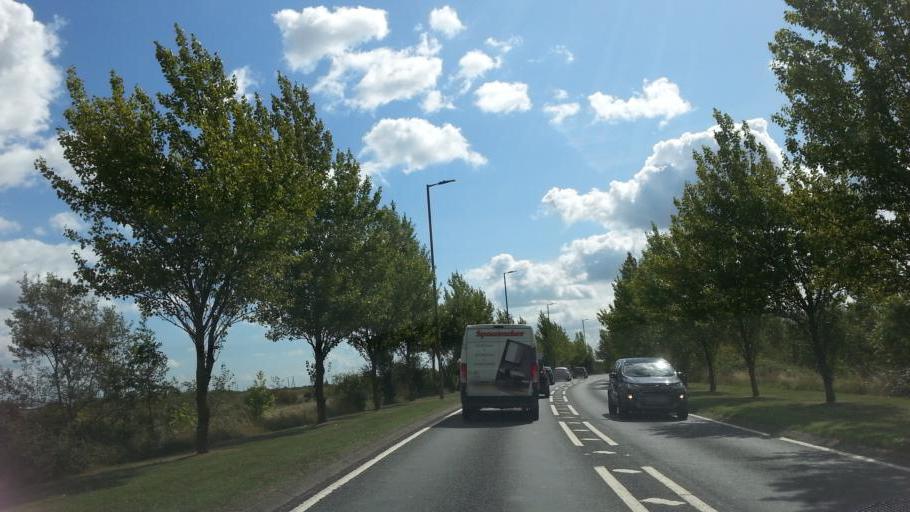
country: GB
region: England
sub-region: Essex
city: South Benfleet
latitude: 51.5395
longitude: 0.5592
